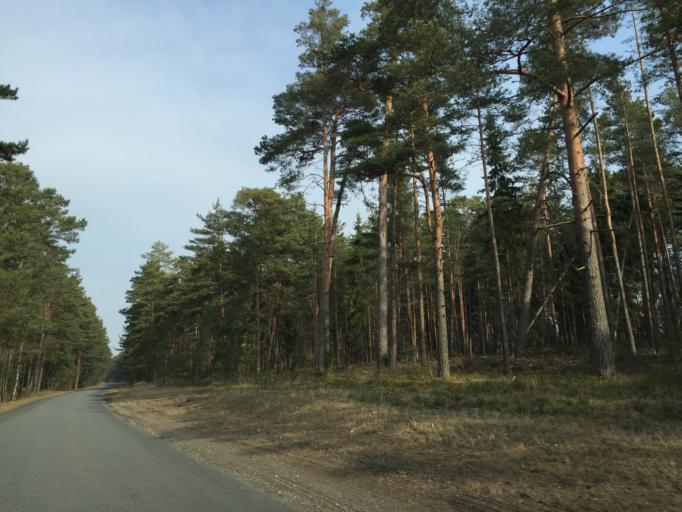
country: LV
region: Salacgrivas
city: Ainazi
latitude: 57.9073
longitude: 24.3807
